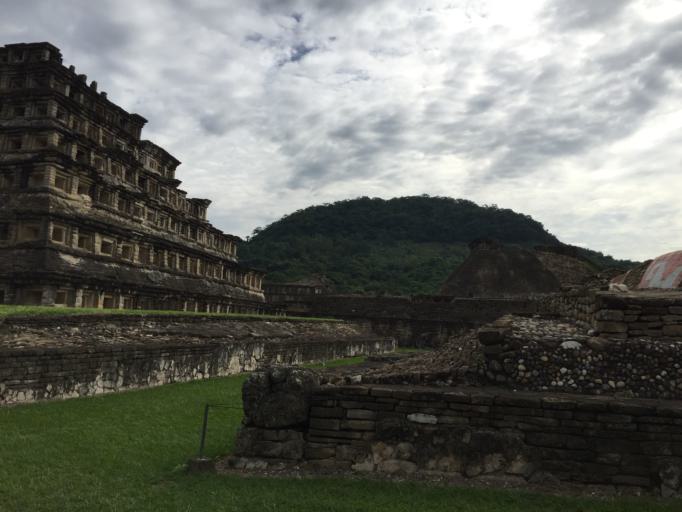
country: MX
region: Veracruz
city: Papantla de Olarte
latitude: 20.4478
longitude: -97.3787
